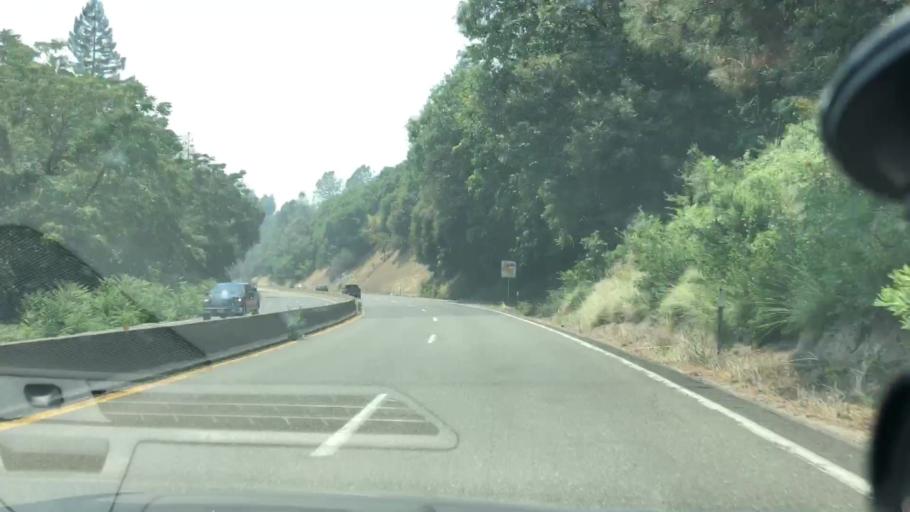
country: US
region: California
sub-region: El Dorado County
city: Placerville
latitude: 38.7388
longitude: -120.7374
